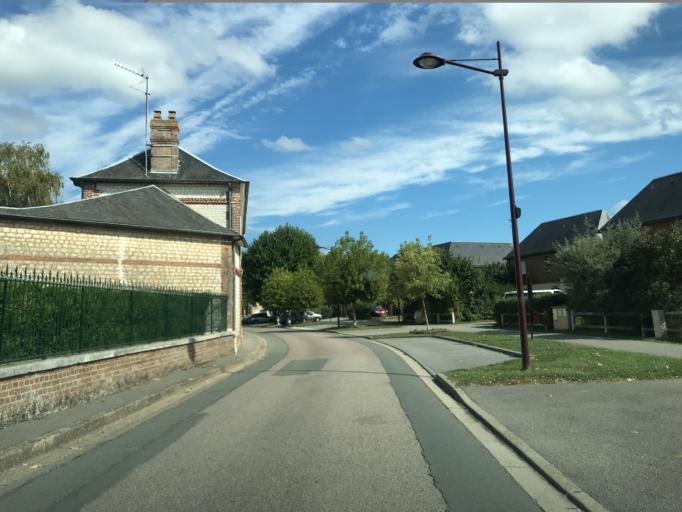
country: FR
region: Haute-Normandie
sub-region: Departement de l'Eure
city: Le Vaudreuil
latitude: 49.2548
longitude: 1.2029
